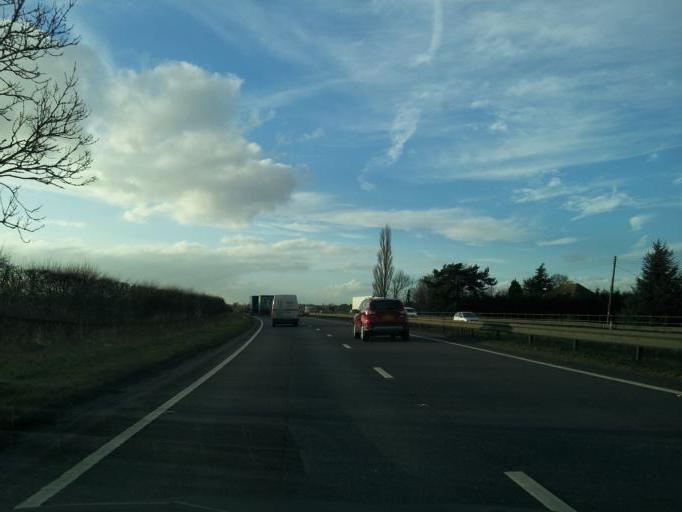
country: GB
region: England
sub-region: Peterborough
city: Wansford
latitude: 52.5747
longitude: -0.4024
